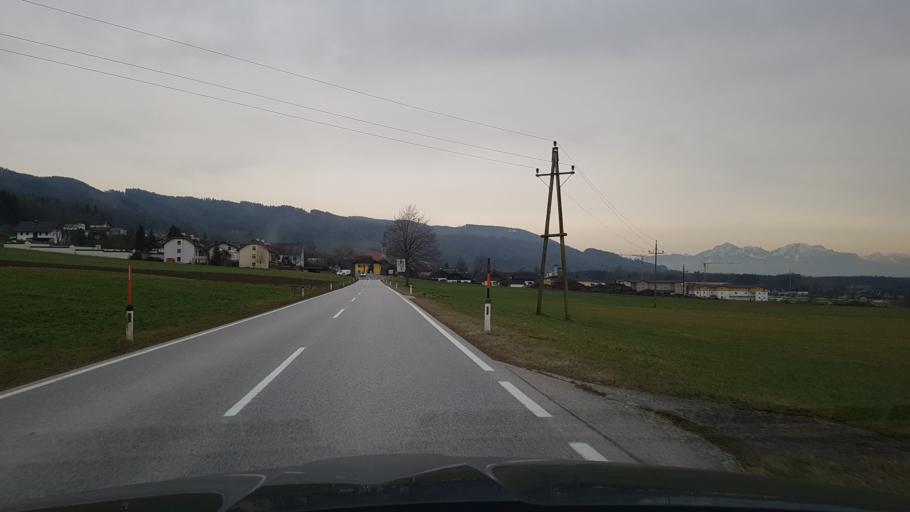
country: AT
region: Salzburg
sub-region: Politischer Bezirk Salzburg-Umgebung
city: Nussdorf am Haunsberg
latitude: 47.9660
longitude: 13.0086
